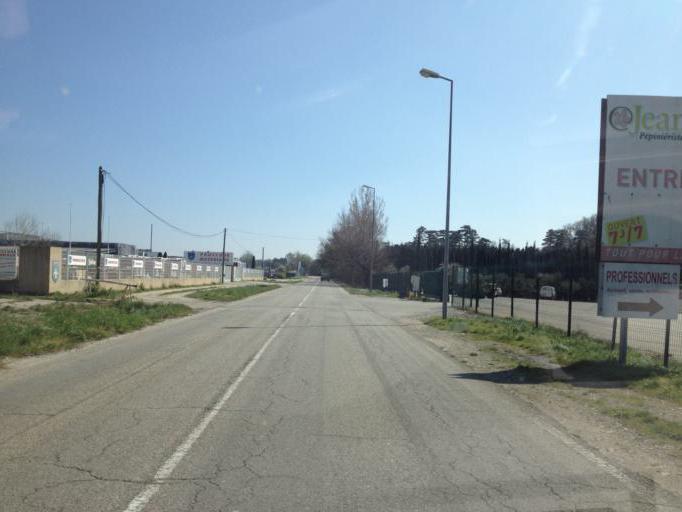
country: FR
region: Provence-Alpes-Cote d'Azur
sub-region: Departement du Vaucluse
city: Jonquieres
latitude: 44.1114
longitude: 4.9116
